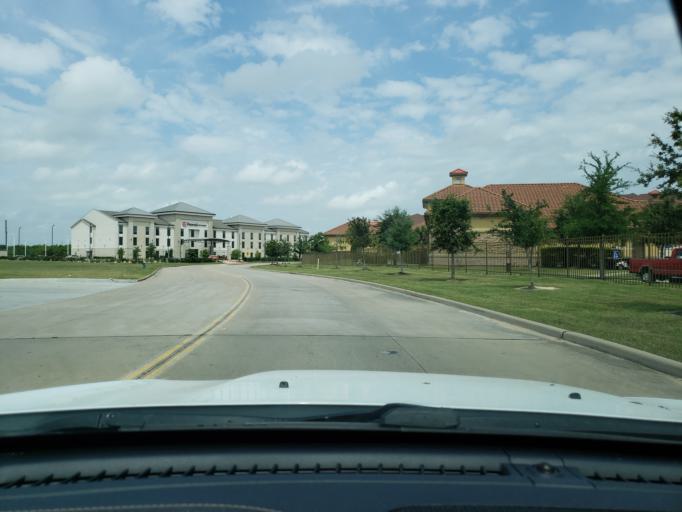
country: US
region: Texas
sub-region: Fort Bend County
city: Cinco Ranch
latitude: 29.7877
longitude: -95.7297
